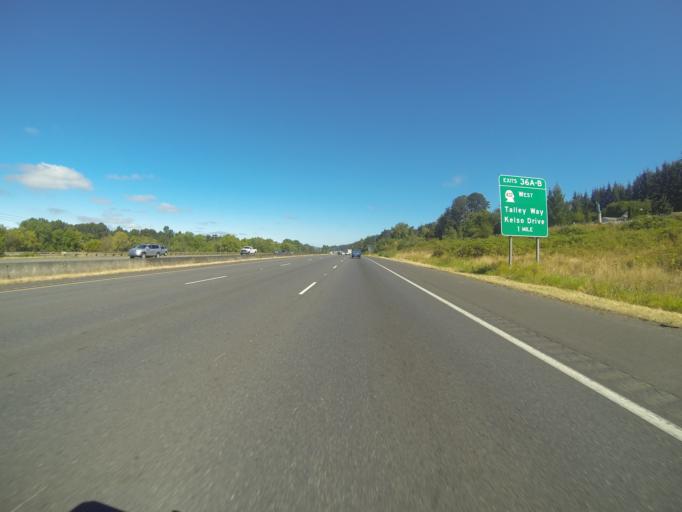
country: US
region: Oregon
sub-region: Columbia County
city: Rainier
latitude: 46.0861
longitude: -122.8683
